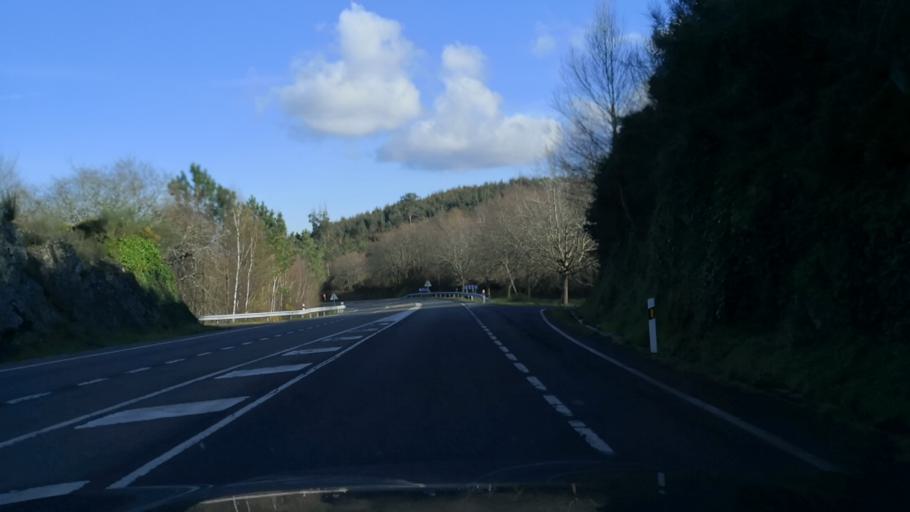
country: ES
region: Galicia
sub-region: Provincia de Pontevedra
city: Silleda
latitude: 42.6983
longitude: -8.3327
